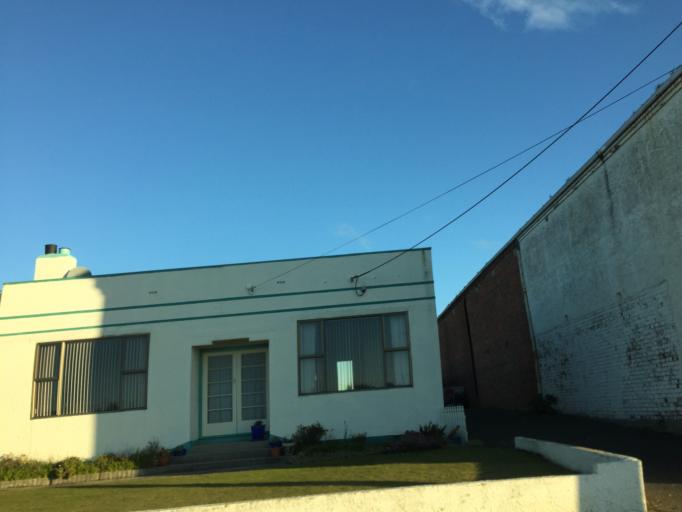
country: NZ
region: Southland
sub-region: Invercargill City
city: Bluff
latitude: -46.5984
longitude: 168.3382
